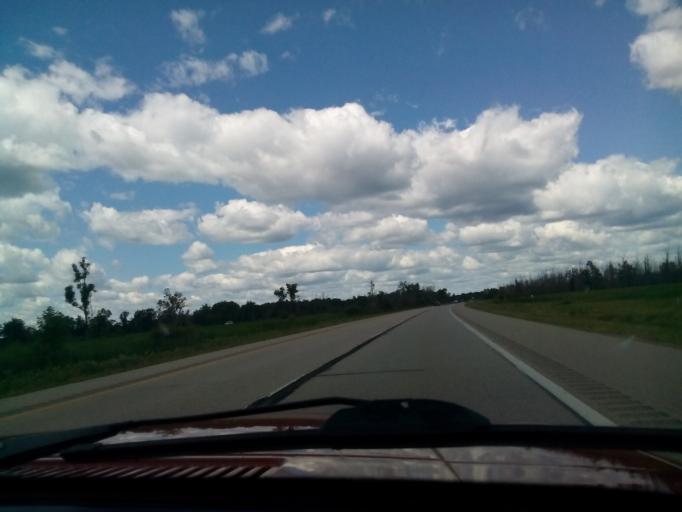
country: US
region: Michigan
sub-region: Ogemaw County
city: Skidway Lake
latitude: 44.0879
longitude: -84.1047
